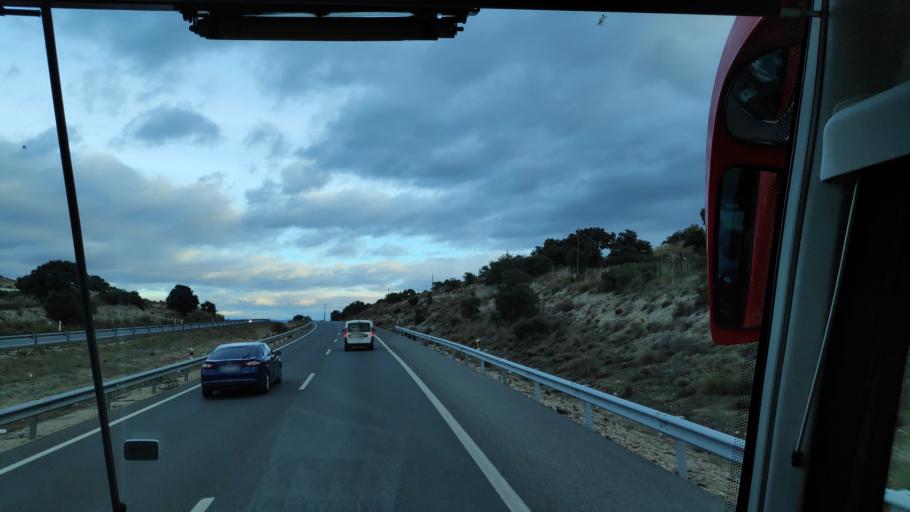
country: ES
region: Madrid
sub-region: Provincia de Madrid
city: Fuentiduena de Tajo
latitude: 40.1408
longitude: -3.2045
